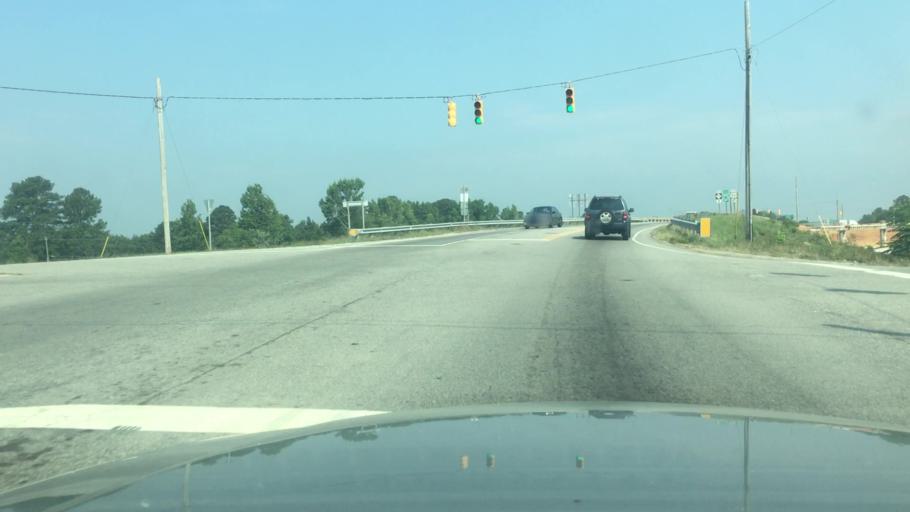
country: US
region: North Carolina
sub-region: Cumberland County
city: Hope Mills
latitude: 34.9438
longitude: -78.9299
